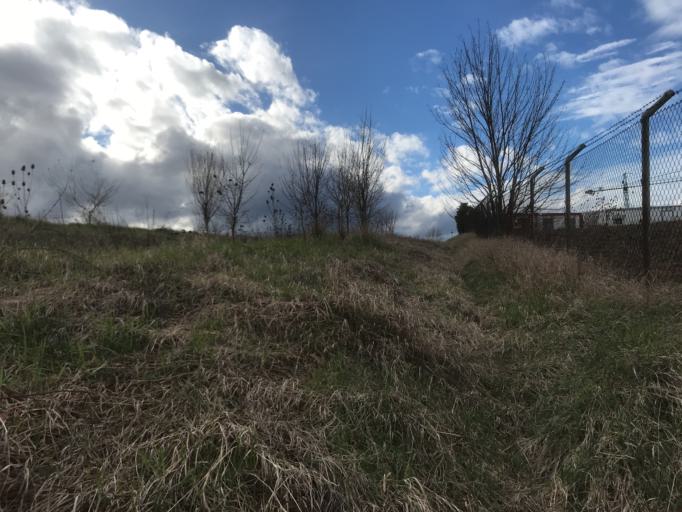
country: ES
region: Basque Country
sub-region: Provincia de Alava
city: Gasteiz / Vitoria
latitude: 42.8309
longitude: -2.6676
